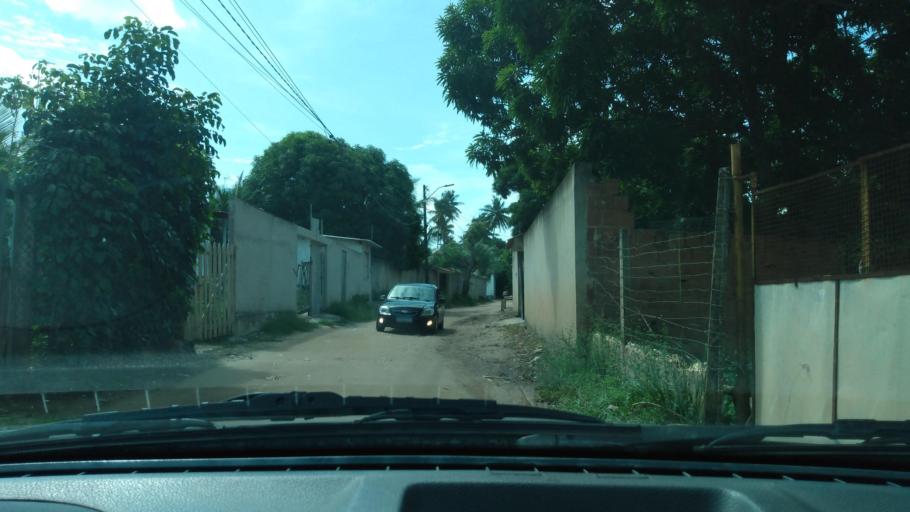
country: BR
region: Pernambuco
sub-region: Cabo De Santo Agostinho
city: Cabo
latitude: -8.3513
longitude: -34.9640
